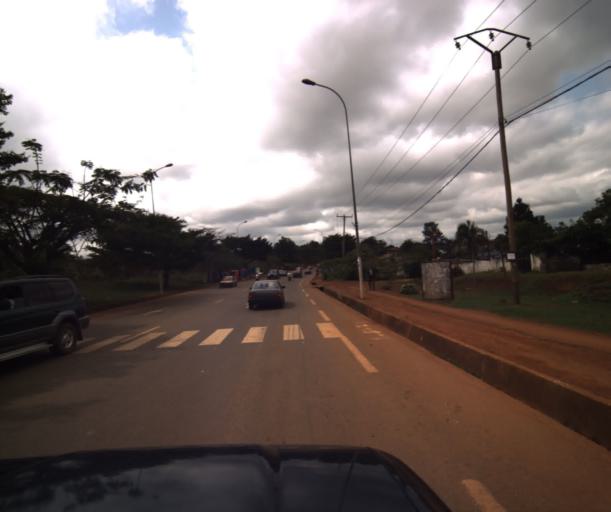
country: CM
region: Centre
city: Yaounde
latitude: 3.8309
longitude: 11.5188
